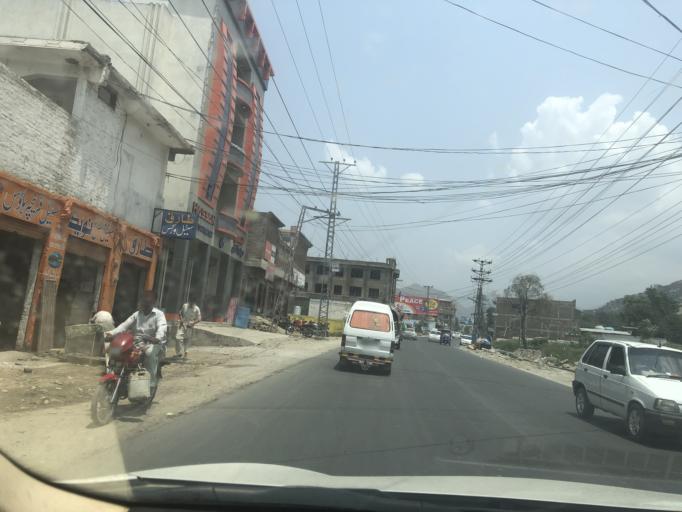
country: PK
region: Khyber Pakhtunkhwa
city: Mingora
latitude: 34.7685
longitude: 72.3337
